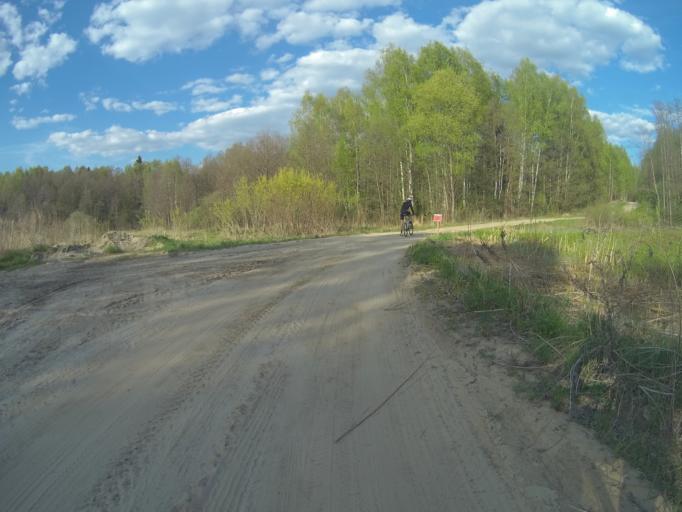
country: RU
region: Vladimir
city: Raduzhnyy
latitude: 55.9979
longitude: 40.2495
